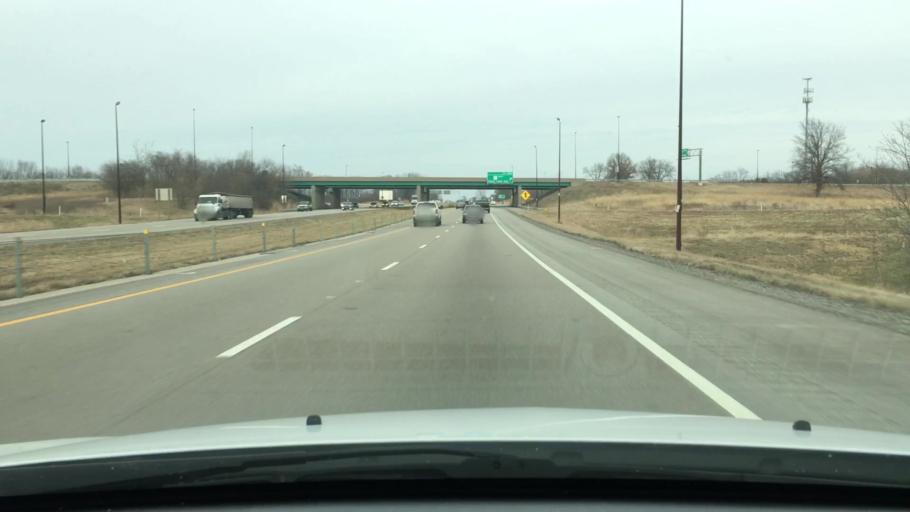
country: US
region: Illinois
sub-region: Sangamon County
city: Grandview
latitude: 39.7997
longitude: -89.5957
